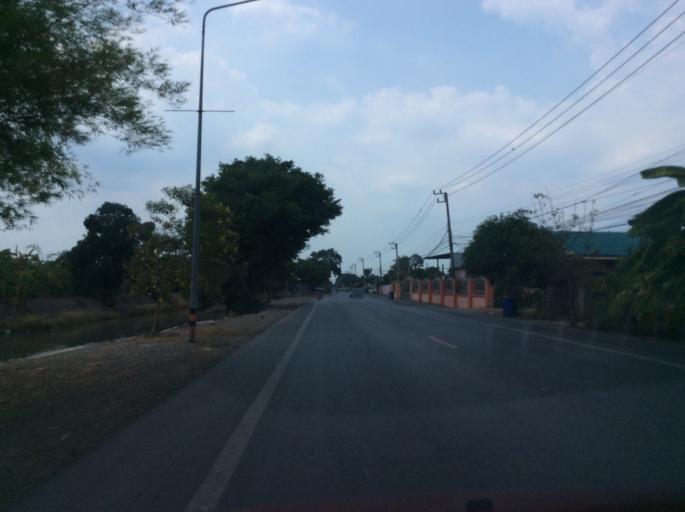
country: TH
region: Pathum Thani
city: Lam Luk Ka
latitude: 13.9578
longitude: 100.7274
